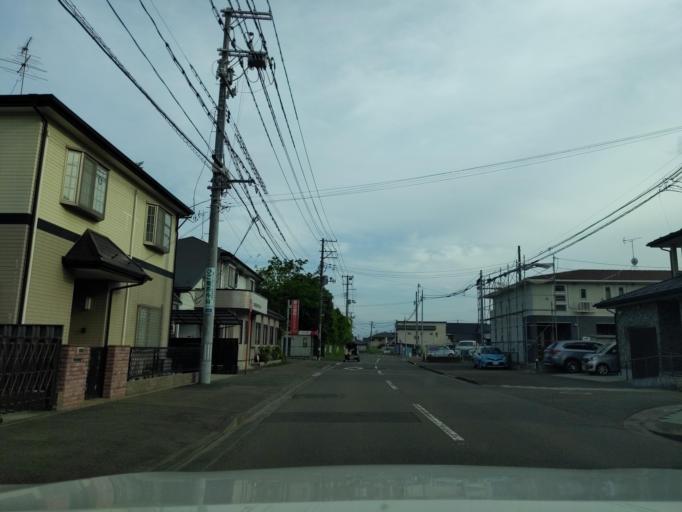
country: JP
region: Miyagi
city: Sendai
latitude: 38.2234
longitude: 140.8915
